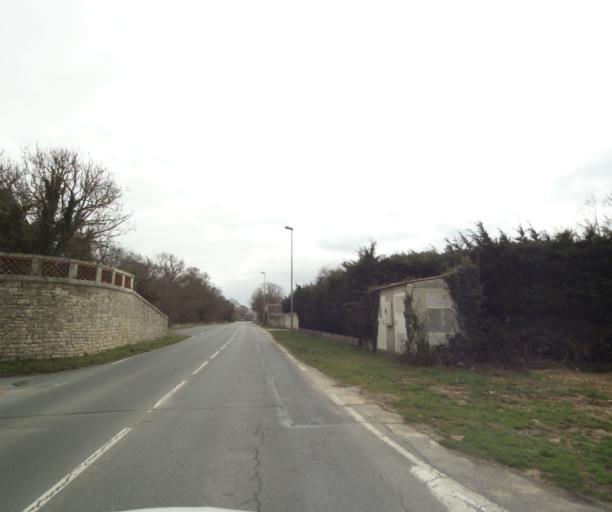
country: FR
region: Poitou-Charentes
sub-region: Departement de la Charente-Maritime
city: Nieul-sur-Mer
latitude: 46.1858
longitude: -1.1781
